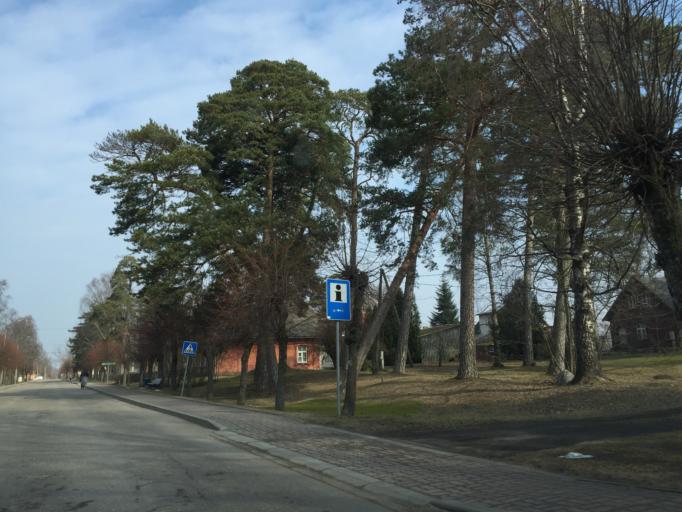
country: LV
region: Salacgrivas
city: Ainazi
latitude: 57.8616
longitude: 24.3580
